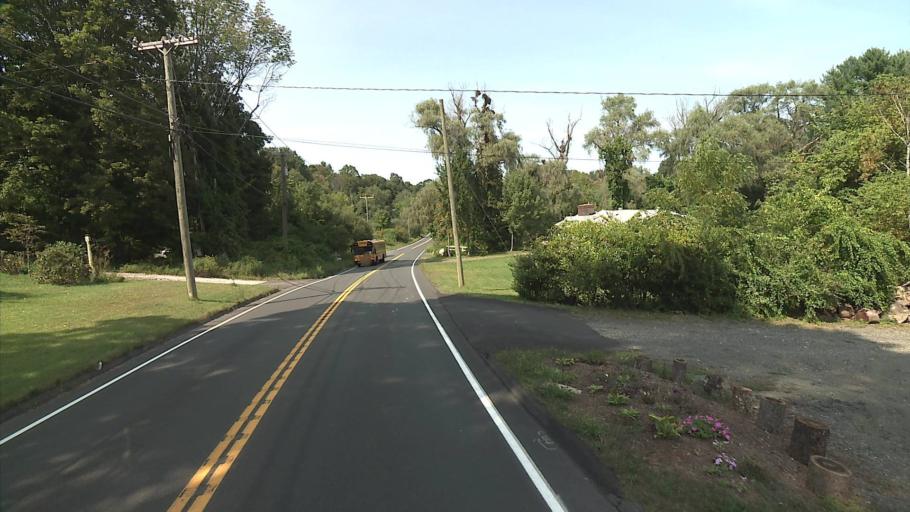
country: US
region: Connecticut
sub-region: Fairfield County
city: Bethel
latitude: 41.3659
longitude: -73.3885
